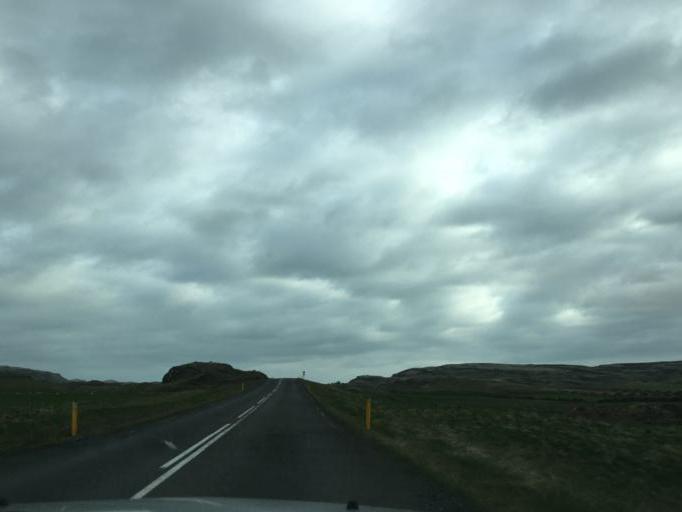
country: IS
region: South
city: Vestmannaeyjar
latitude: 64.2098
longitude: -20.2684
